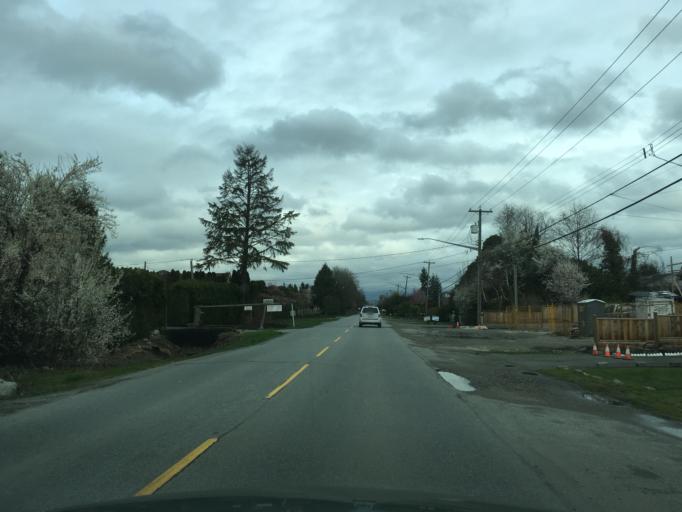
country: CA
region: British Columbia
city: Richmond
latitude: 49.1633
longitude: -123.0692
